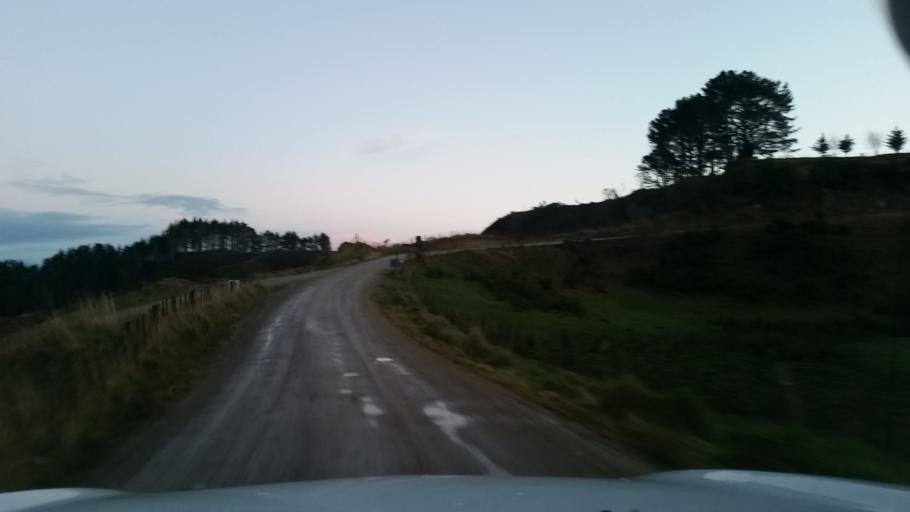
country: NZ
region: Manawatu-Wanganui
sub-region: Wanganui District
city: Wanganui
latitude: -39.7724
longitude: 174.8707
